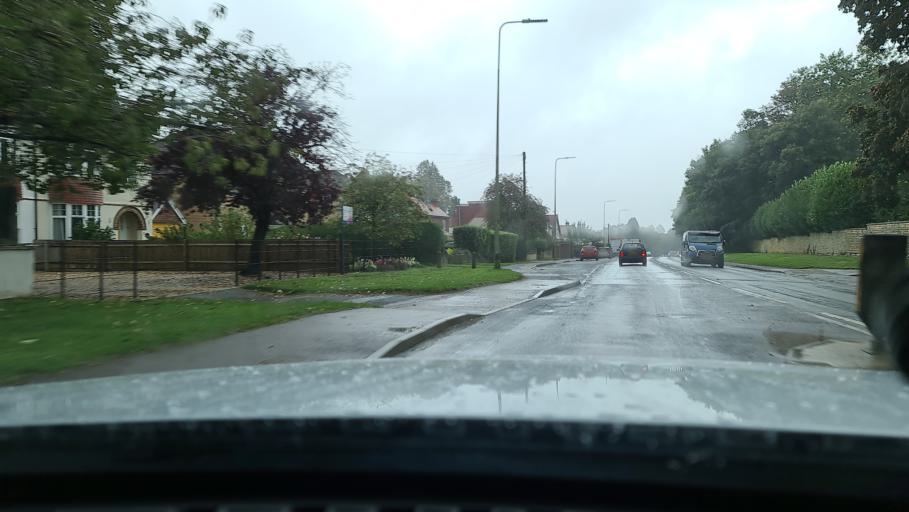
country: GB
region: England
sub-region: Oxfordshire
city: Adderbury
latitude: 52.0253
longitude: -1.3120
